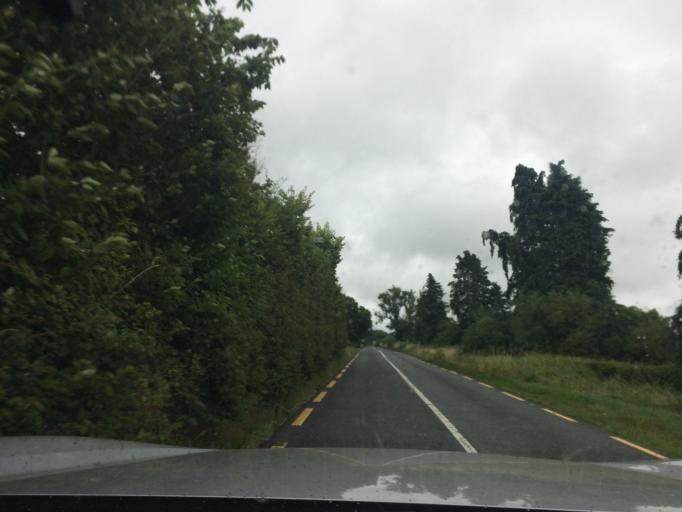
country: IE
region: Munster
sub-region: South Tipperary
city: Cluain Meala
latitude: 52.2922
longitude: -7.7716
